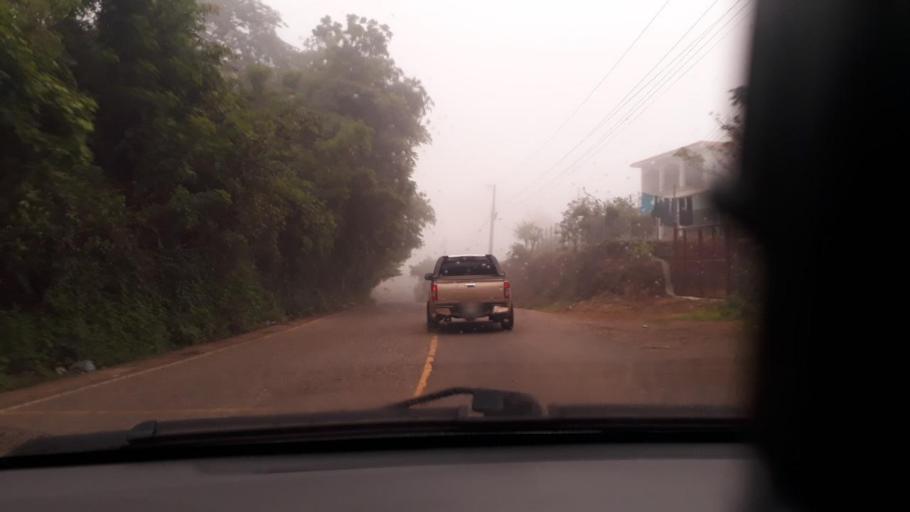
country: GT
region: Jutiapa
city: Jalpatagua
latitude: 14.1797
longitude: -90.0246
